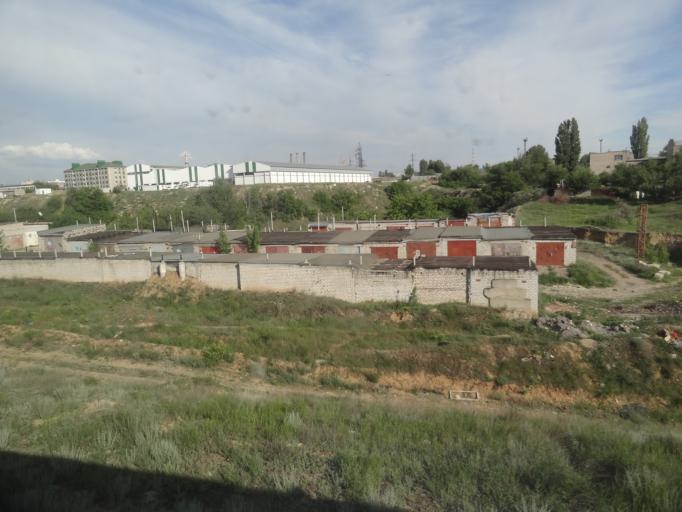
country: RU
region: Volgograd
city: Gorodishche
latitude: 48.7716
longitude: 44.4546
